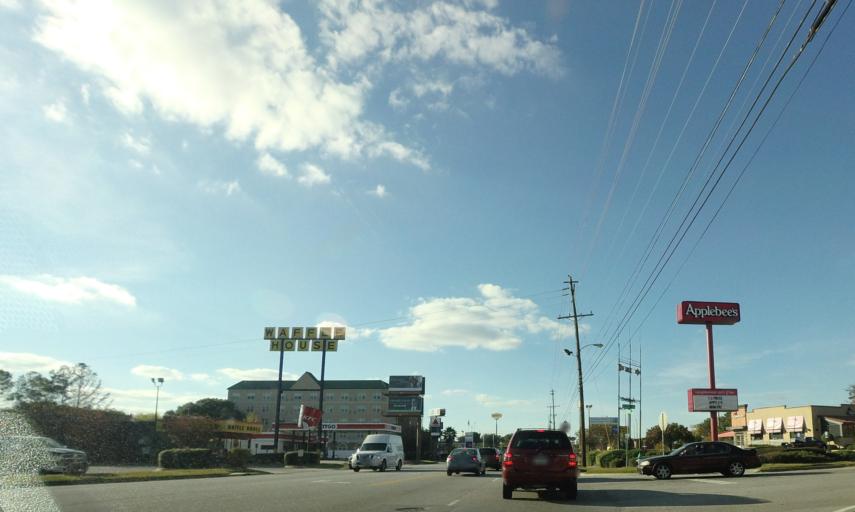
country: US
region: Georgia
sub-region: Lowndes County
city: Remerton
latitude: 30.8425
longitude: -83.3260
